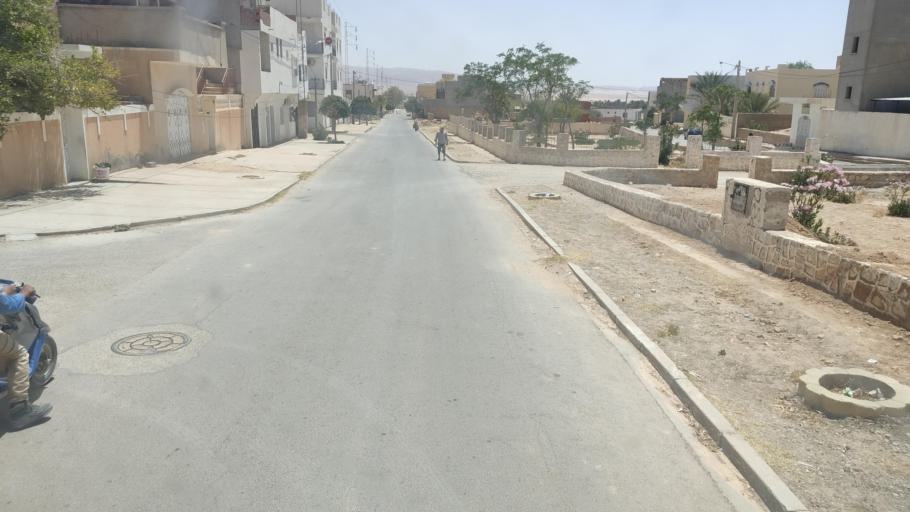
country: TN
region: Gafsa
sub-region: Gafsa Municipality
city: Gafsa
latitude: 34.3405
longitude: 8.9424
